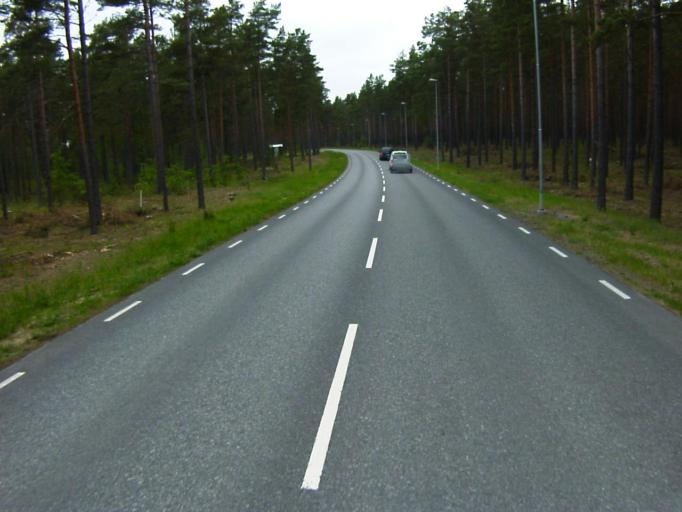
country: SE
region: Skane
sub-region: Kristianstads Kommun
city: Ahus
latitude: 55.9486
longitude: 14.2967
